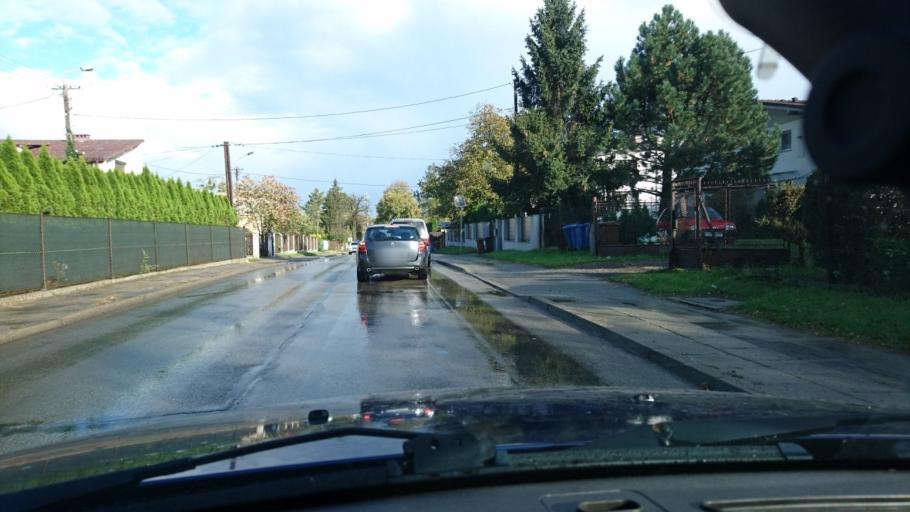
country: PL
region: Silesian Voivodeship
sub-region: Bielsko-Biala
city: Bielsko-Biala
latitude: 49.8557
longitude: 19.0307
